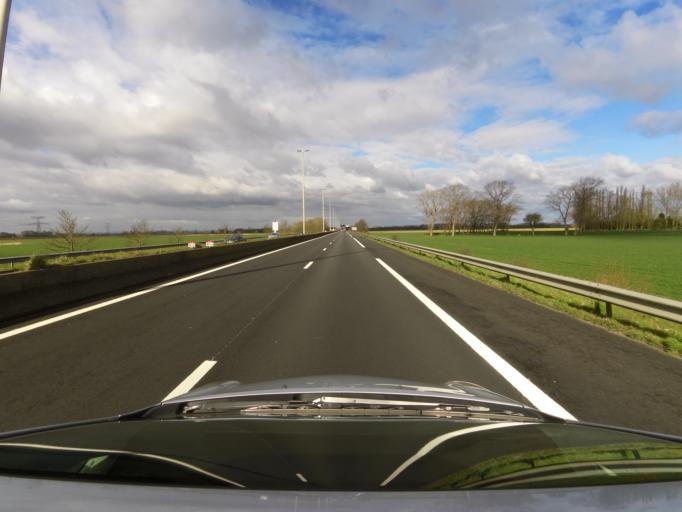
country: FR
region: Nord-Pas-de-Calais
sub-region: Departement du Pas-de-Calais
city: Marck
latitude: 50.9341
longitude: 1.9916
